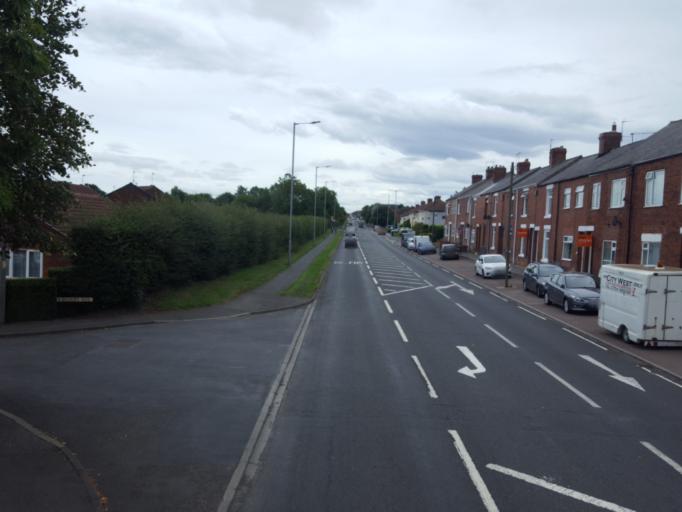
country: GB
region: England
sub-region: County Durham
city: Durham
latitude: 54.8023
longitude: -1.5888
